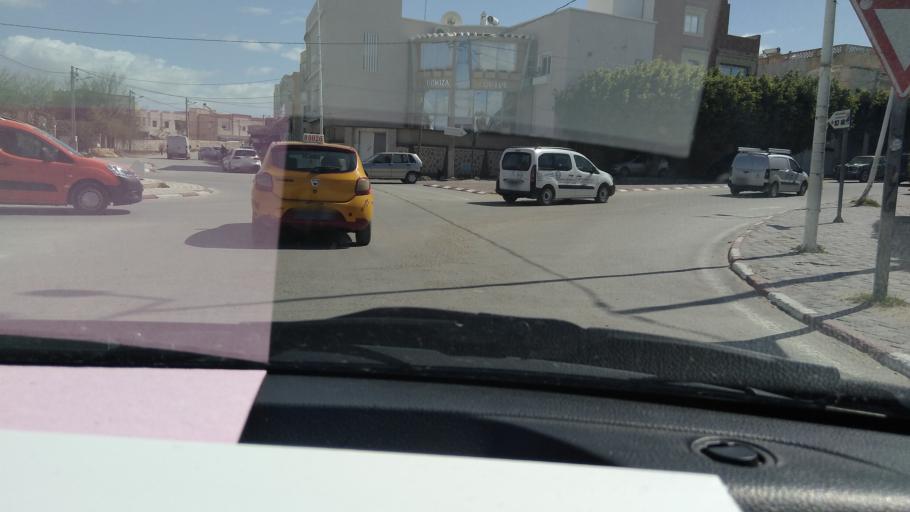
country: TN
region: Al Qayrawan
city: Kairouan
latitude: 35.6811
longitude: 10.0912
